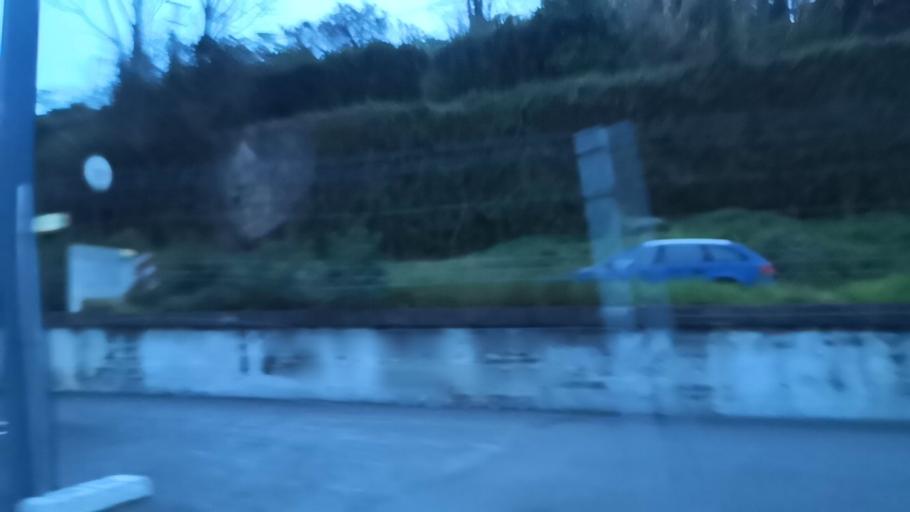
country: PT
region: Porto
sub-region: Vila Nova de Gaia
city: Oliveira do Douro
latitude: 41.1426
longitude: -8.5873
